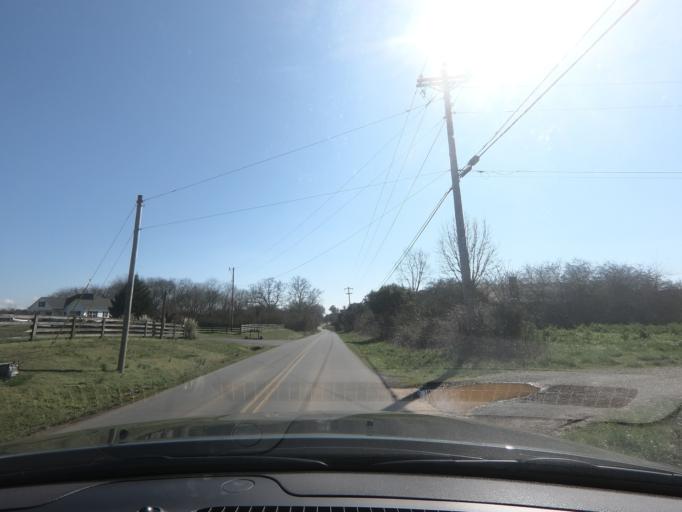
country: US
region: Georgia
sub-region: Bartow County
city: Rydal
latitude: 34.4458
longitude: -84.8091
